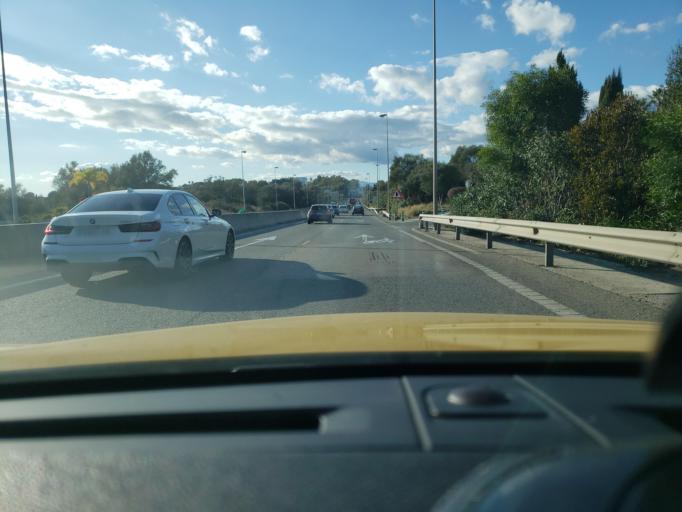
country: ES
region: Andalusia
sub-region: Provincia de Malaga
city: Ojen
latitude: 36.5059
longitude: -4.8146
